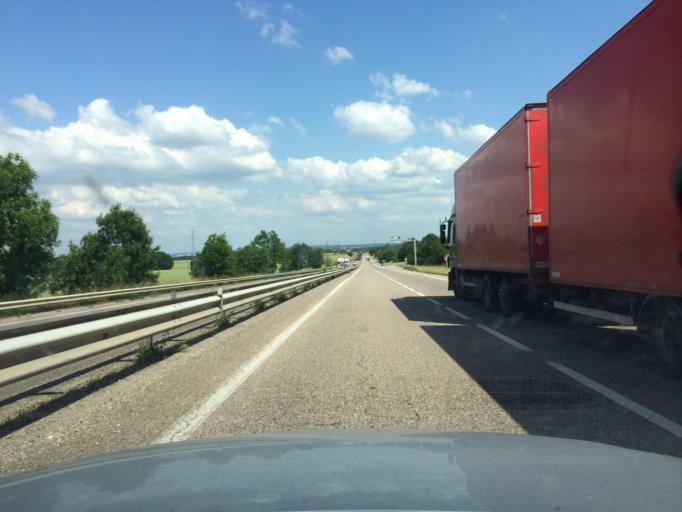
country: FR
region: Lorraine
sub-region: Departement de Meurthe-et-Moselle
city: Foug
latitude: 48.6697
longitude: 5.8059
